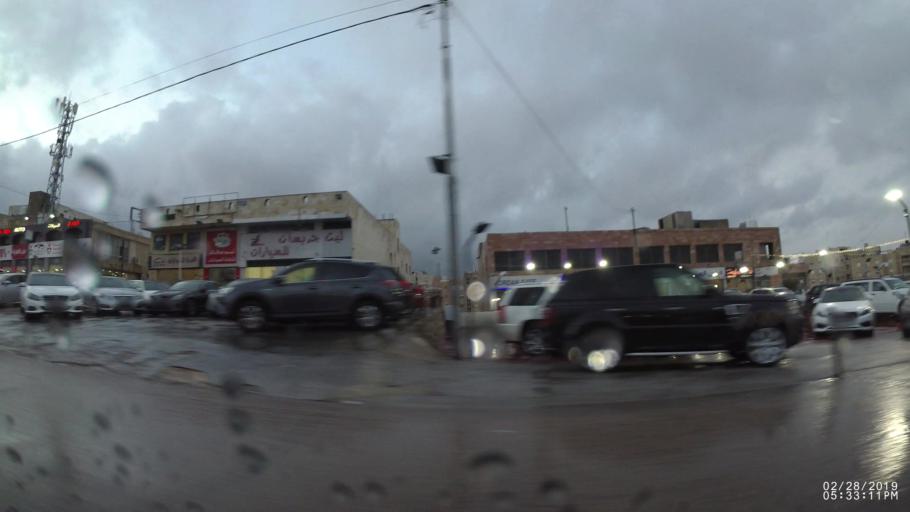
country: JO
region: Amman
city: Amman
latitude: 31.9921
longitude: 35.9137
